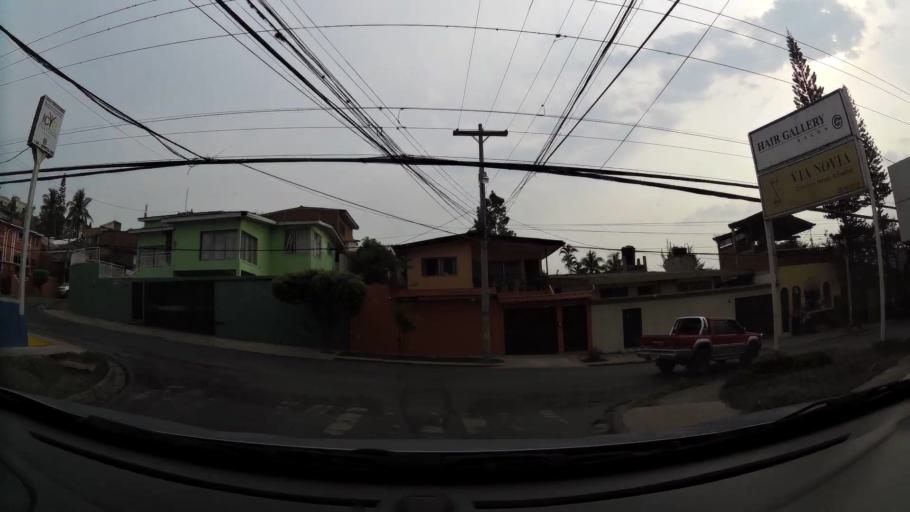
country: HN
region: Francisco Morazan
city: Tegucigalpa
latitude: 14.0840
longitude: -87.1979
